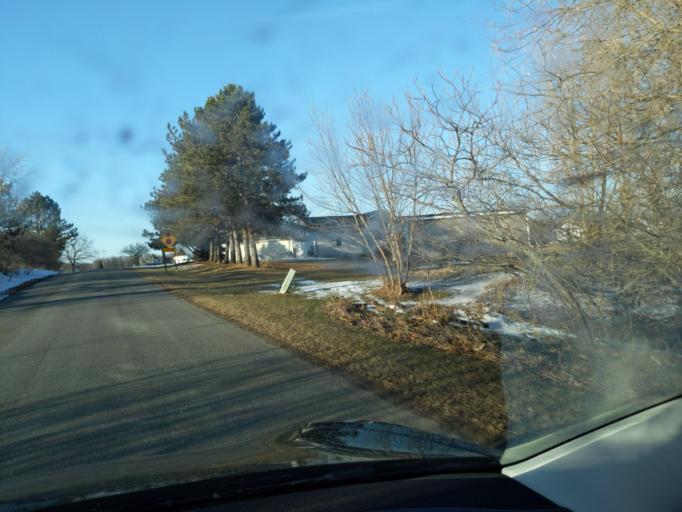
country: US
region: Michigan
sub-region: Ingham County
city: Stockbridge
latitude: 42.5176
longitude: -84.2443
